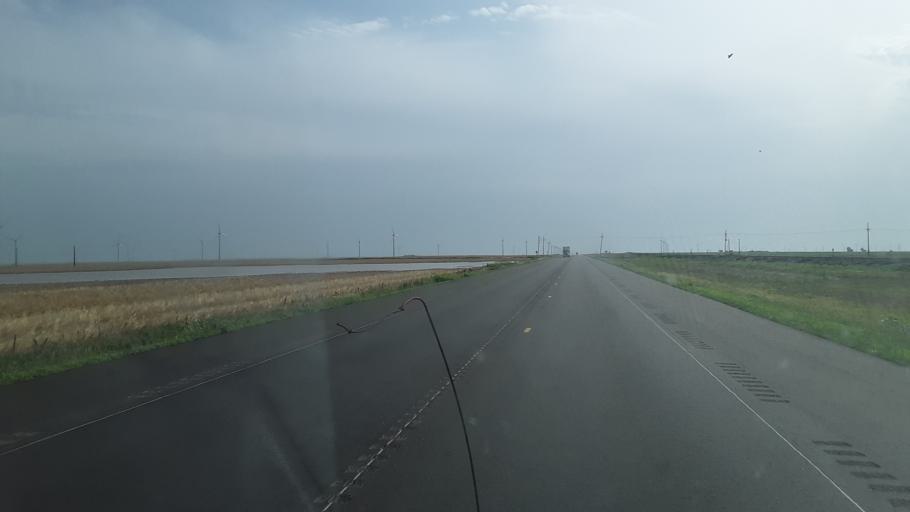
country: US
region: Kansas
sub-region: Ford County
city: Dodge City
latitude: 37.7921
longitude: -99.8736
